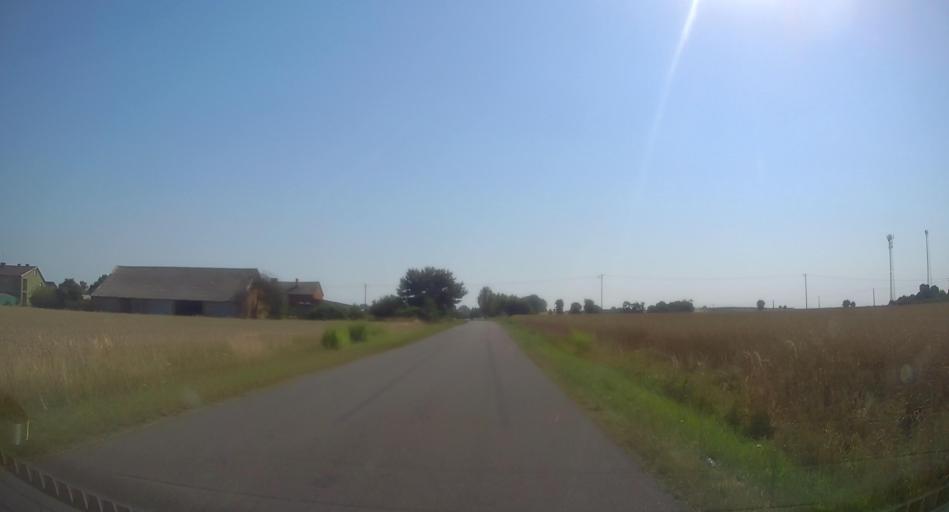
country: PL
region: Lodz Voivodeship
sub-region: Powiat skierniewicki
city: Kaweczyn Nowy
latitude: 51.8803
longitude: 20.2172
